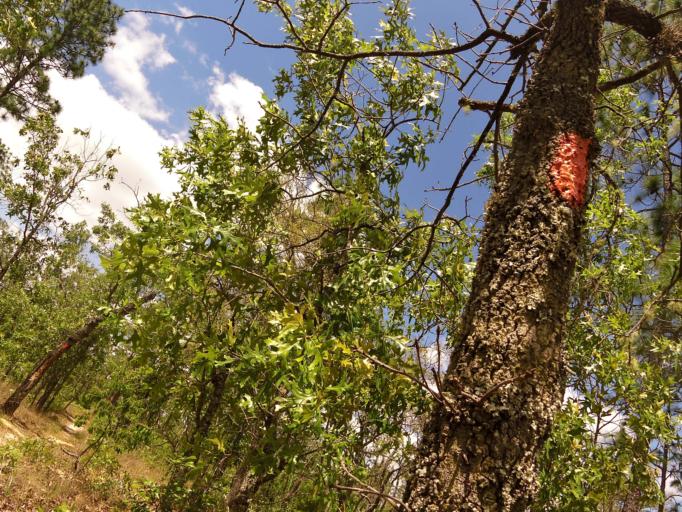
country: US
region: Florida
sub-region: Clay County
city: Keystone Heights
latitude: 29.8416
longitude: -81.9636
